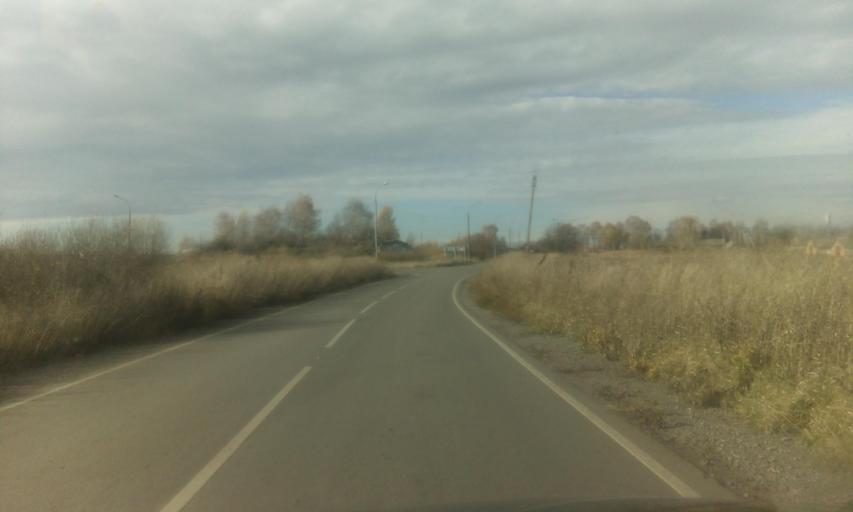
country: RU
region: Tula
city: Dubovka
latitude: 53.9410
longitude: 38.0248
